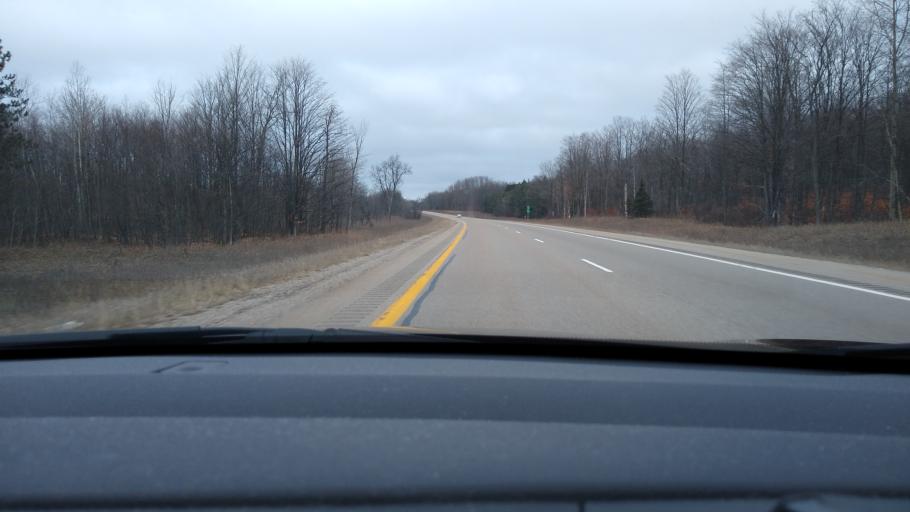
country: US
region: Michigan
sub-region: Crawford County
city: Grayling
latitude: 44.8165
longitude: -84.7116
